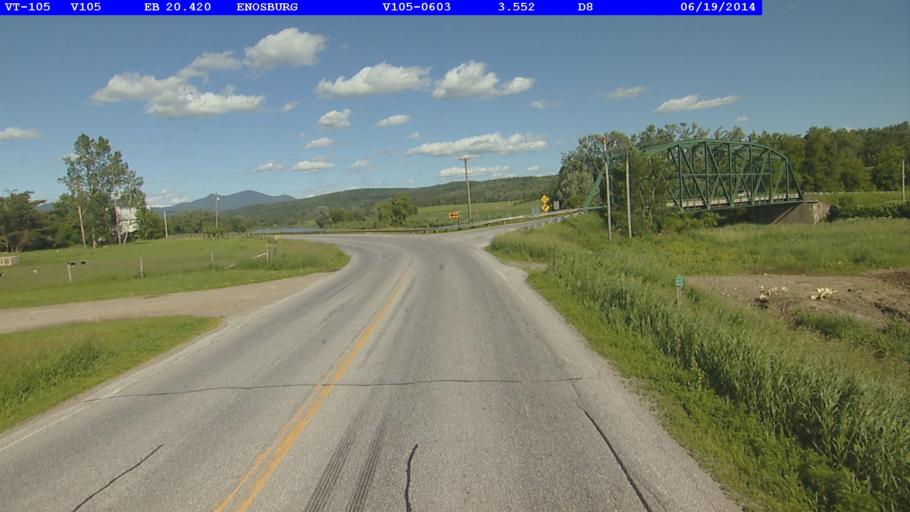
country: US
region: Vermont
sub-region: Franklin County
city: Enosburg Falls
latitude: 44.9205
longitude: -72.7577
